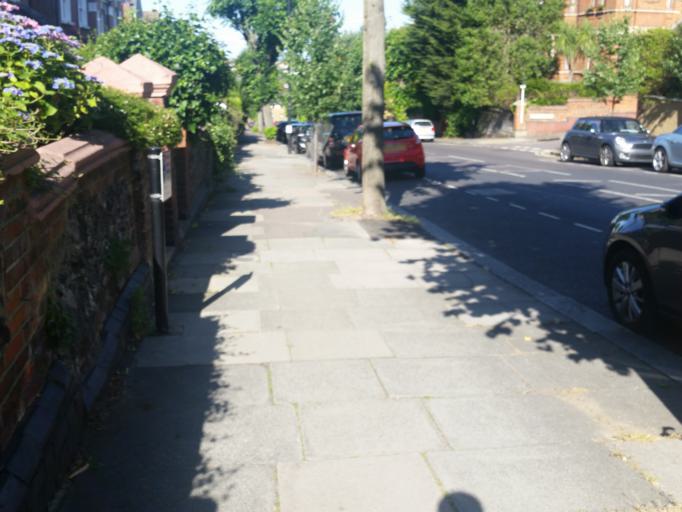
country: GB
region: England
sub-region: Greater London
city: Crouch End
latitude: 51.5801
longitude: -0.1309
